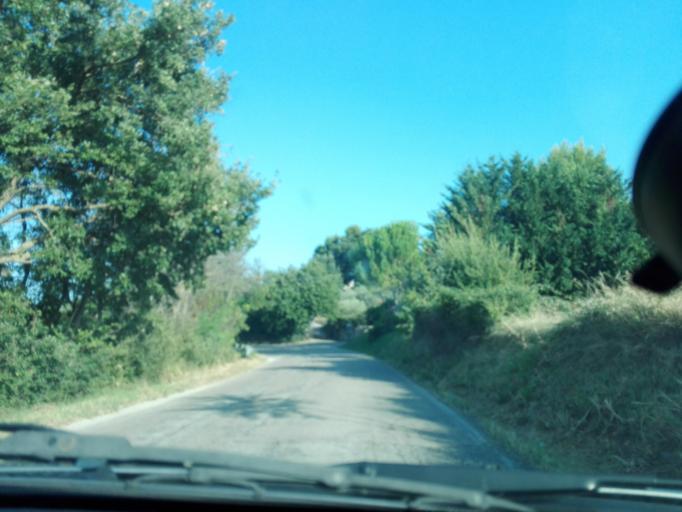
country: IT
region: Abruzzo
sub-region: Provincia di Pescara
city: Cappelle sul Tavo
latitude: 42.4445
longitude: 14.0924
